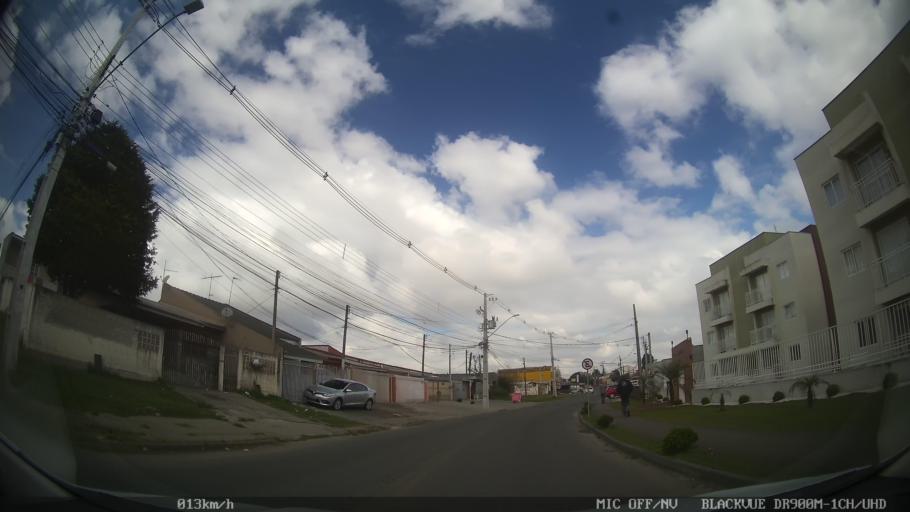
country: BR
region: Parana
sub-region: Colombo
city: Colombo
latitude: -25.3523
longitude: -49.2066
